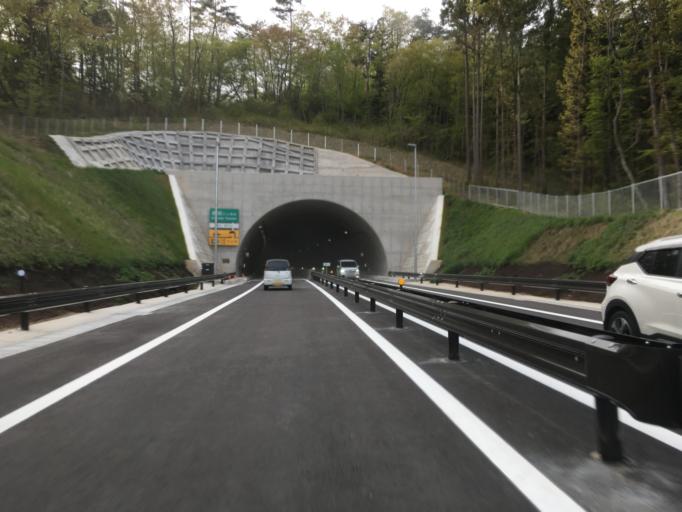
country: JP
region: Fukushima
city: Hobaramachi
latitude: 37.7776
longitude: 140.5804
